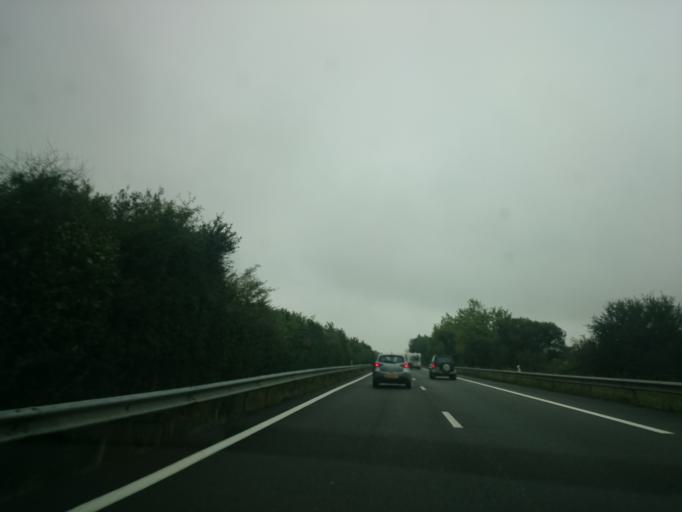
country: FR
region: Pays de la Loire
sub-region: Departement de la Loire-Atlantique
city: Jans
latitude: 47.6000
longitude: -1.6278
